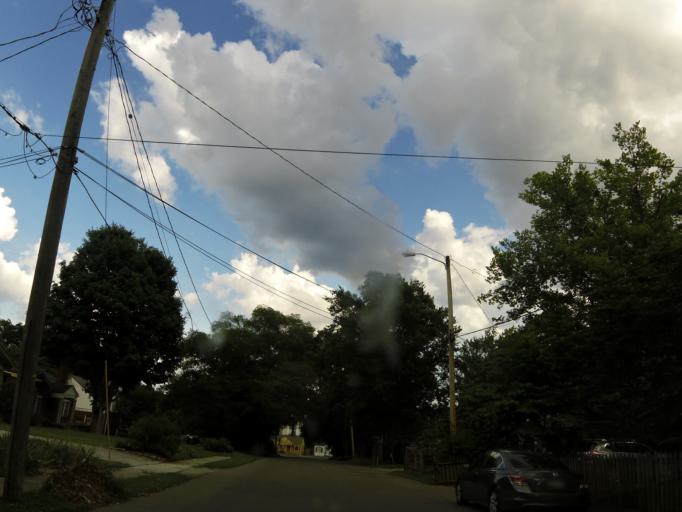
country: US
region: Tennessee
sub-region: Davidson County
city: Nashville
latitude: 36.1860
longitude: -86.7323
